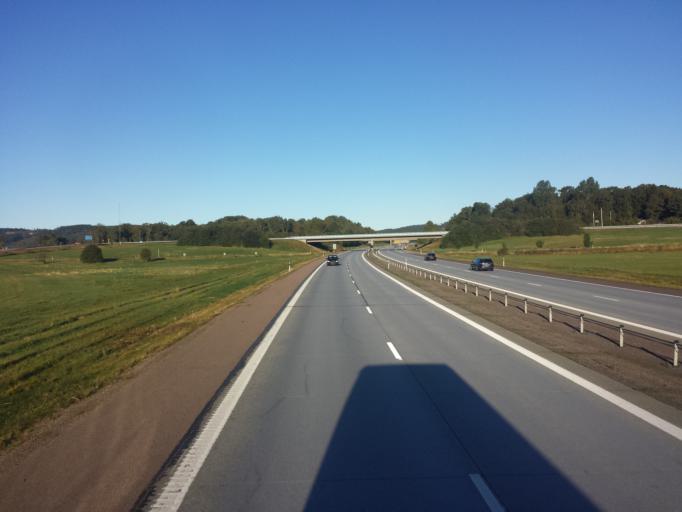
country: SE
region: Halland
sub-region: Halmstads Kommun
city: Getinge
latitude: 56.8059
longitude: 12.7407
